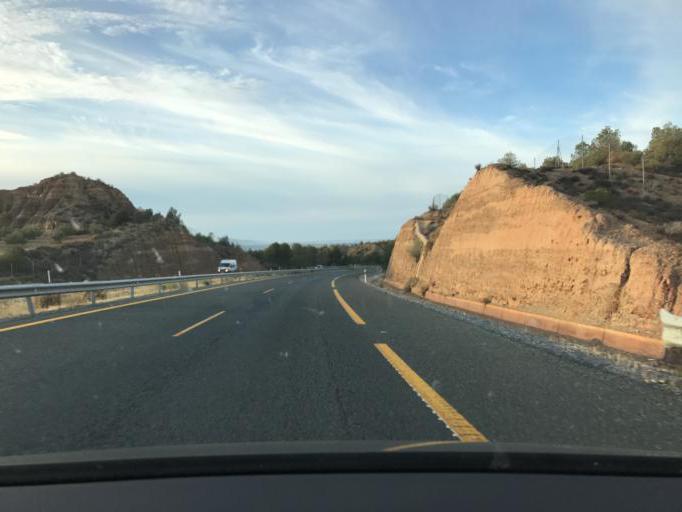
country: ES
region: Andalusia
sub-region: Provincia de Granada
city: Guadix
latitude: 37.2884
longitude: -3.1093
